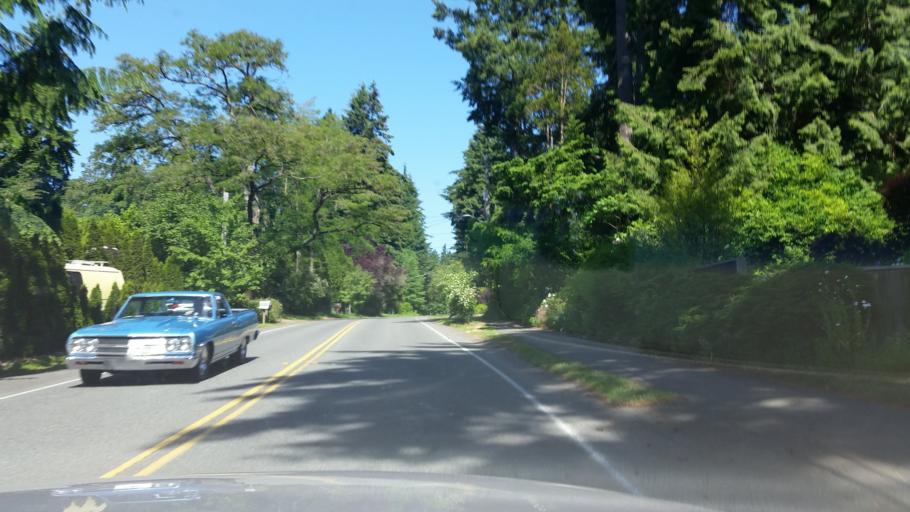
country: US
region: Washington
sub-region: King County
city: Lake Forest Park
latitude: 47.7539
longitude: -122.2839
